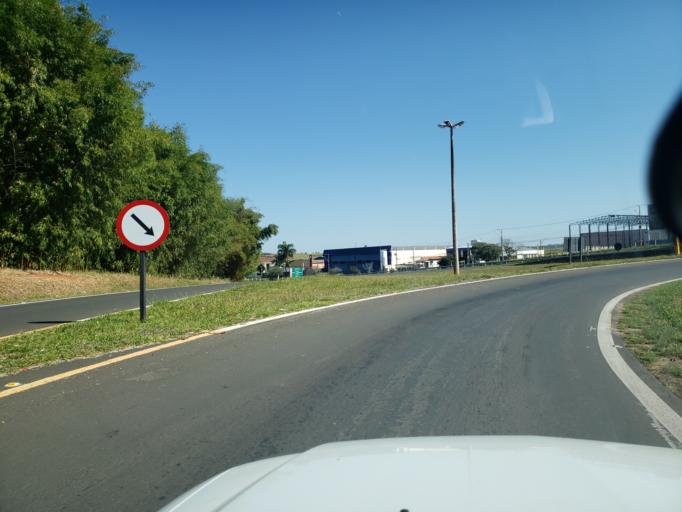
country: BR
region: Sao Paulo
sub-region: Itapira
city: Itapira
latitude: -22.4479
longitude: -46.8333
